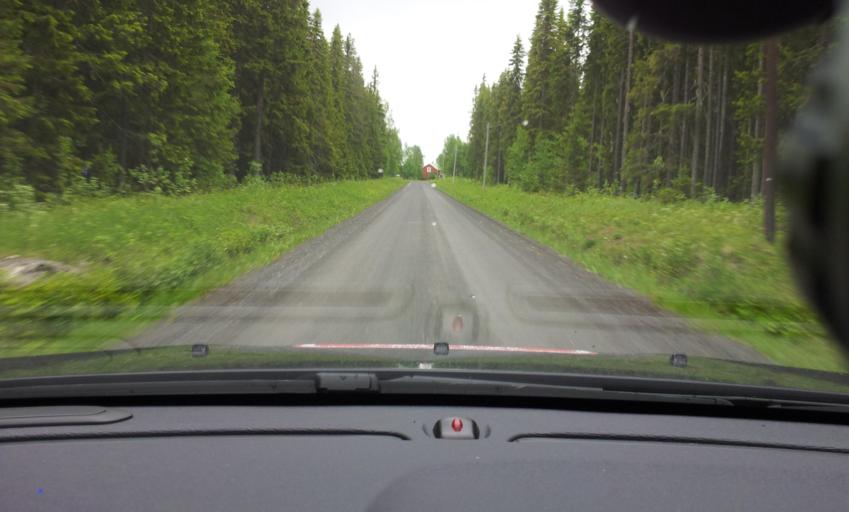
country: SE
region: Jaemtland
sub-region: OEstersunds Kommun
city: Brunflo
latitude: 63.1596
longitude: 15.0103
